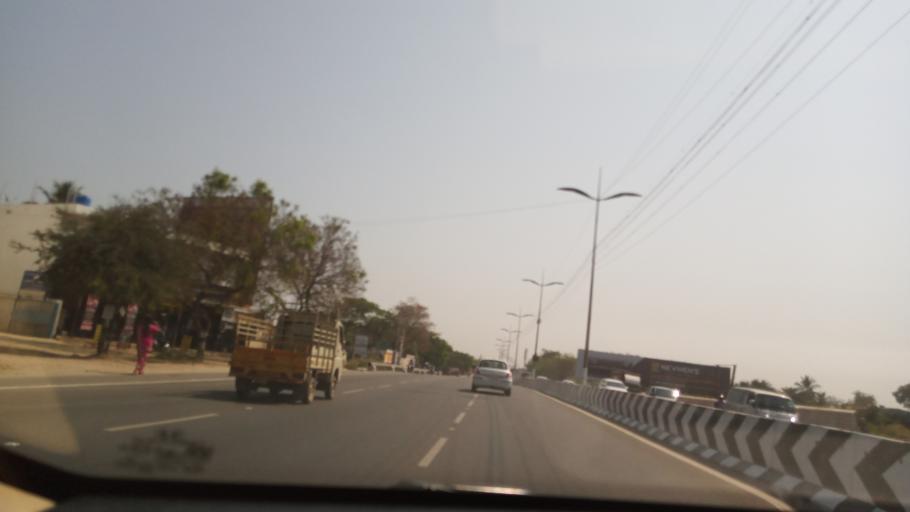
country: IN
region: Tamil Nadu
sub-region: Coimbatore
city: Irugur
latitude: 11.0476
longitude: 77.0542
